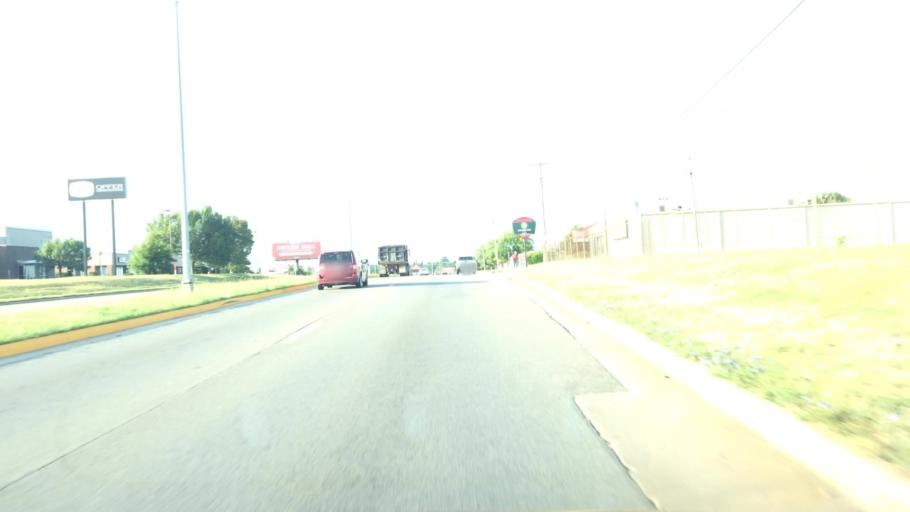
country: US
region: Missouri
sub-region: Greene County
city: Springfield
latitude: 37.1635
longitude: -93.3164
